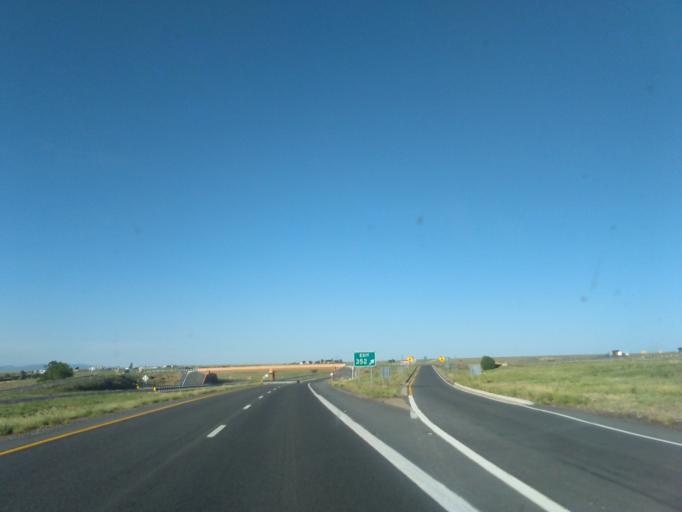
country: US
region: New Mexico
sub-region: San Miguel County
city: Las Vegas
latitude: 35.6764
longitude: -105.1729
